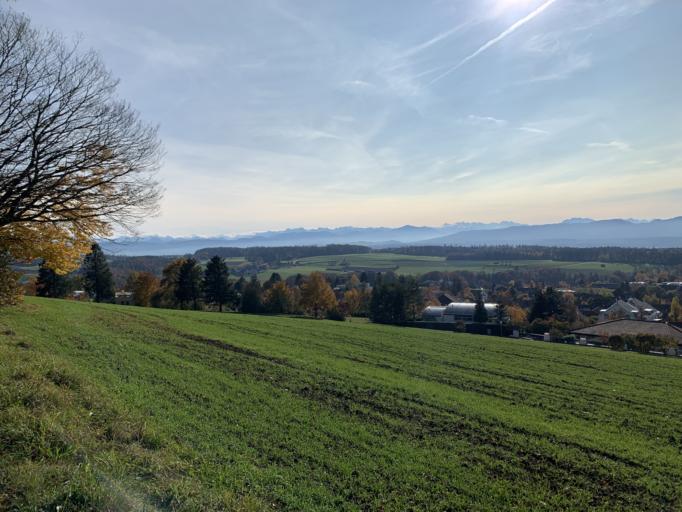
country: CH
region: Zurich
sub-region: Bezirk Meilen
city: Zumikon
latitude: 47.3333
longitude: 8.6295
